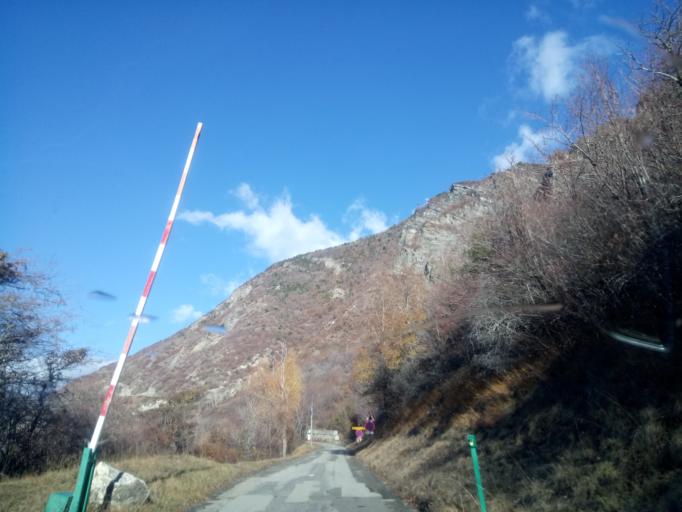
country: FR
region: Rhone-Alpes
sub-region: Departement de la Savoie
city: Villargondran
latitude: 45.2618
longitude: 6.3939
